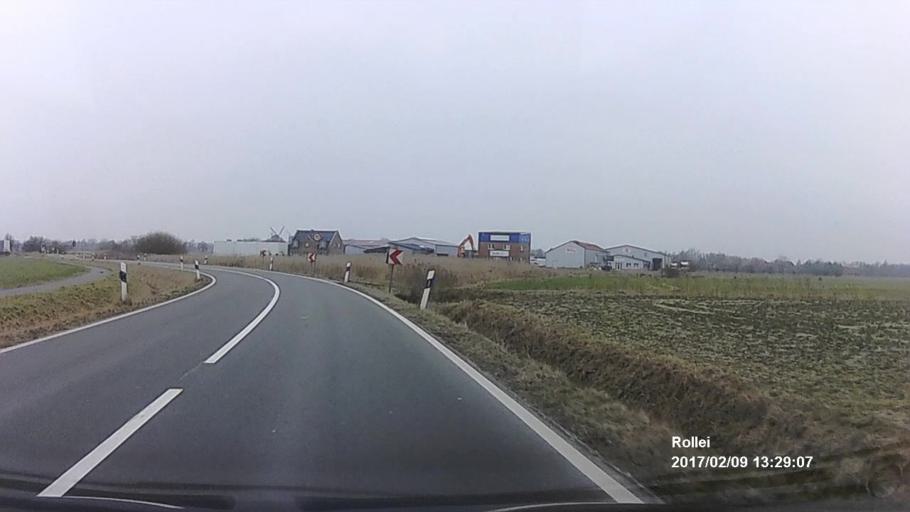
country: DE
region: Lower Saxony
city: Wirdum
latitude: 53.4937
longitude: 7.1110
